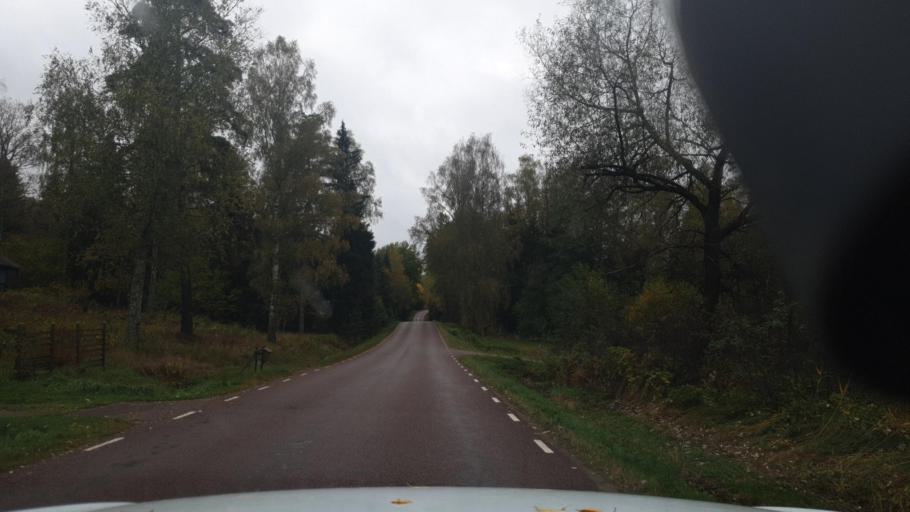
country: SE
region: Vaermland
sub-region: Grums Kommun
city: Grums
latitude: 59.4162
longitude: 13.0828
